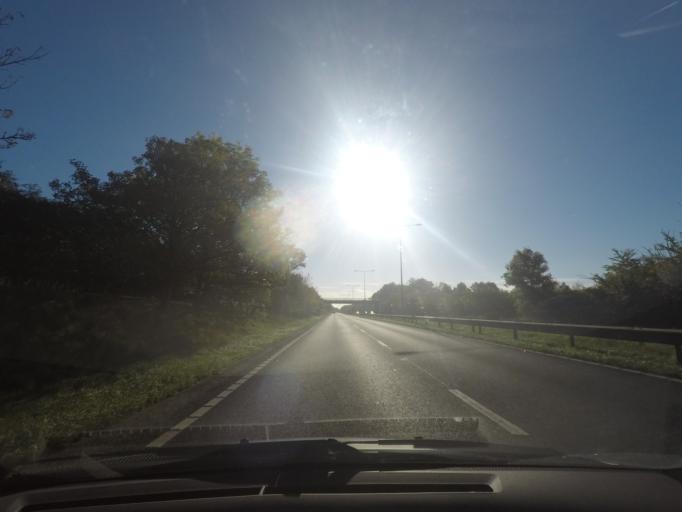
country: GB
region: England
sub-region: East Riding of Yorkshire
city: Brantingham
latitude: 53.7517
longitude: -0.5793
